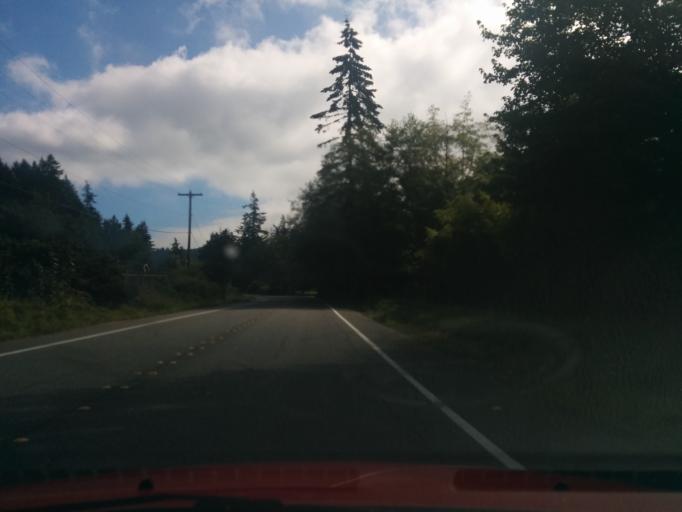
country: US
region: Washington
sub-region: Whatcom County
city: Bellingham
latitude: 48.7096
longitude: -122.4994
